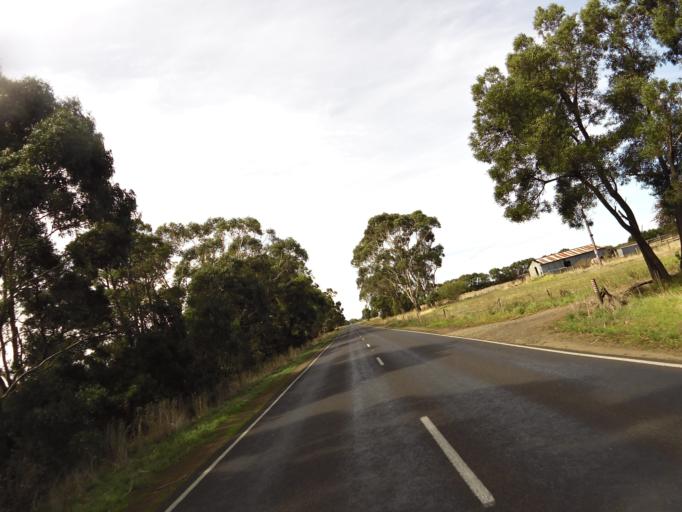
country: AU
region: Victoria
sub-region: Warrnambool
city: Allansford
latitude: -38.3980
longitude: 142.9528
